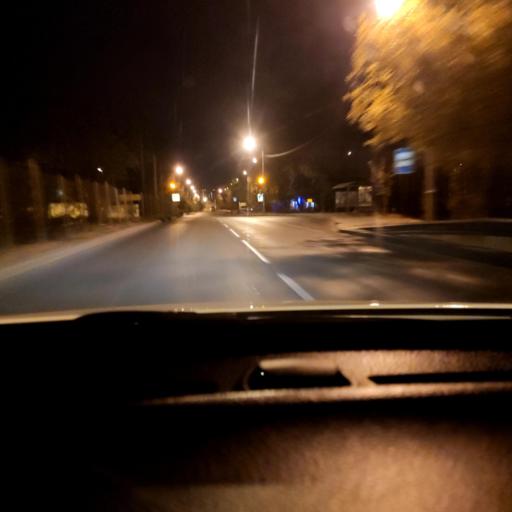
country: RU
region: Voronezj
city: Voronezh
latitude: 51.7049
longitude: 39.2287
